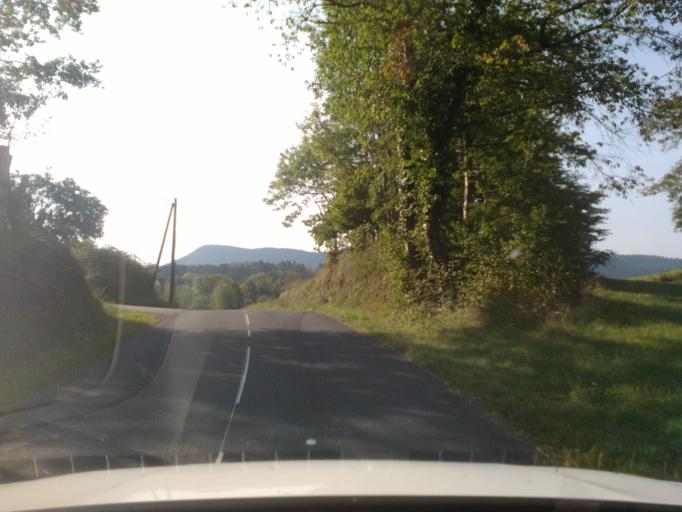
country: FR
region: Lorraine
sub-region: Departement des Vosges
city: Senones
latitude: 48.3489
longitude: 7.0201
